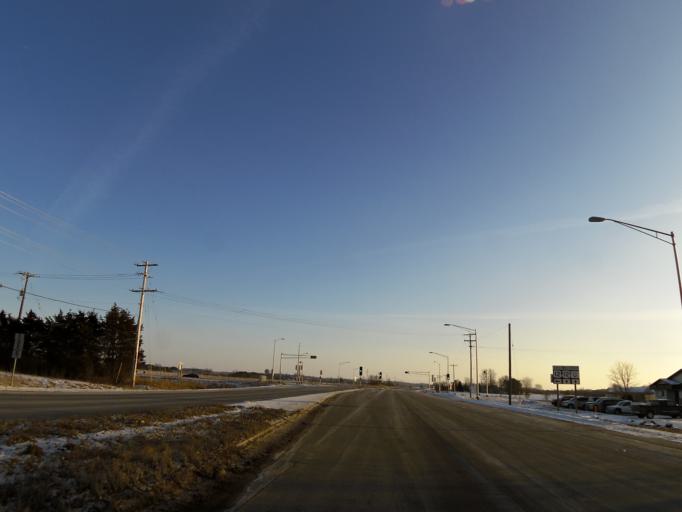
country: US
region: Wisconsin
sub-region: Saint Croix County
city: North Hudson
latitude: 44.9892
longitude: -92.6804
